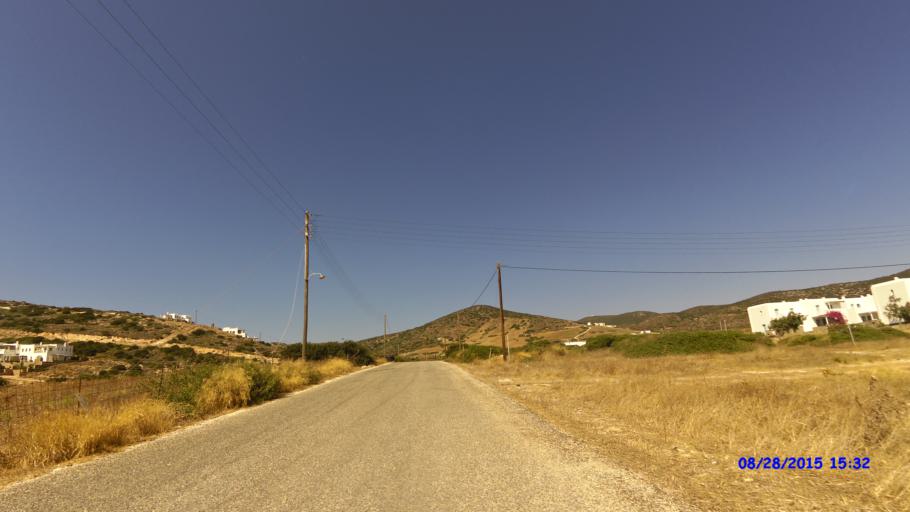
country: GR
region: South Aegean
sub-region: Nomos Kykladon
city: Antiparos
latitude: 36.9784
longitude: 25.0279
